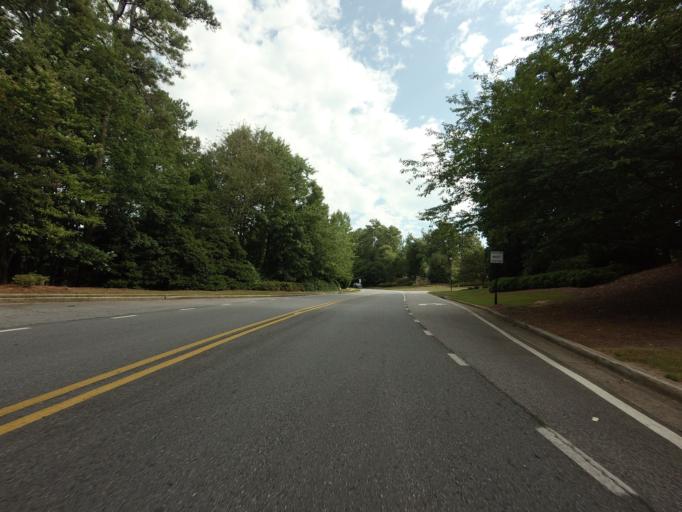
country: US
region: Georgia
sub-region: Gwinnett County
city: Duluth
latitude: 34.0527
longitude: -84.1441
